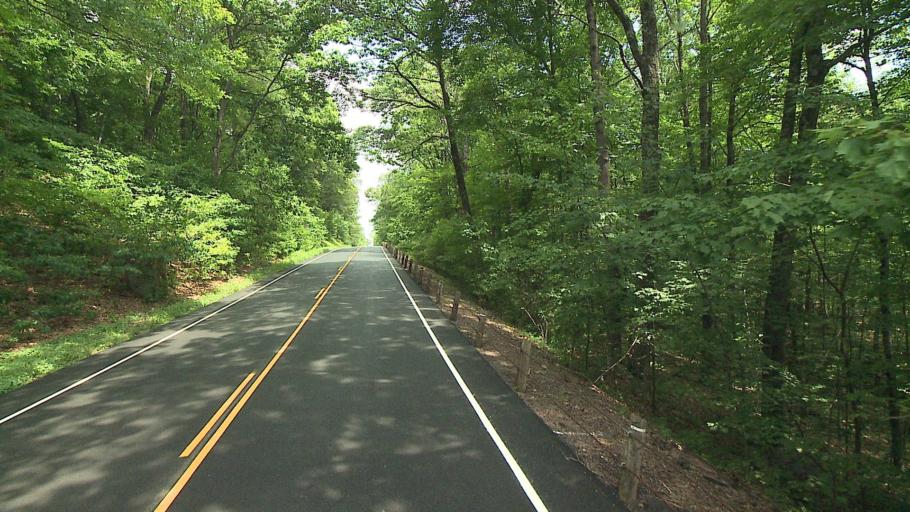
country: US
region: Massachusetts
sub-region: Hampden County
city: Granville
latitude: 42.0209
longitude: -72.8893
